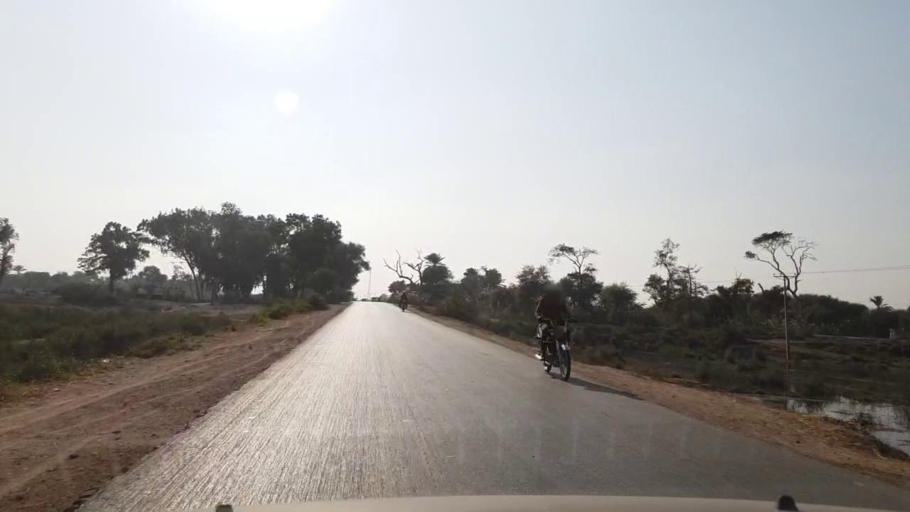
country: PK
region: Sindh
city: Tando Muhammad Khan
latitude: 25.0579
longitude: 68.4589
